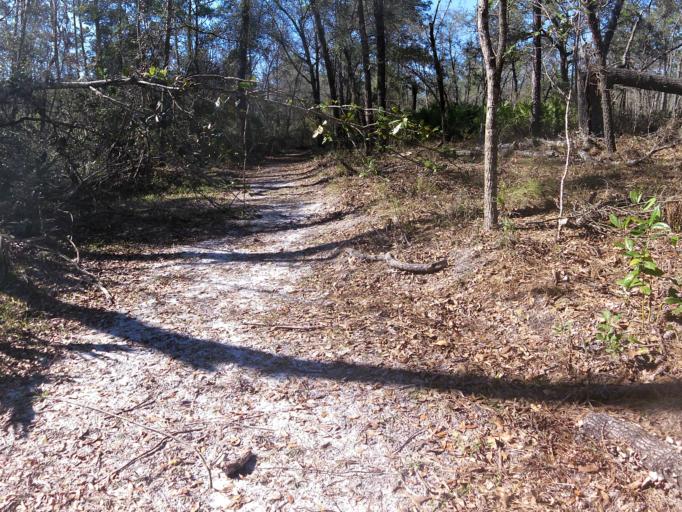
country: US
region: Florida
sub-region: Clay County
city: Middleburg
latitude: 30.1386
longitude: -81.8911
